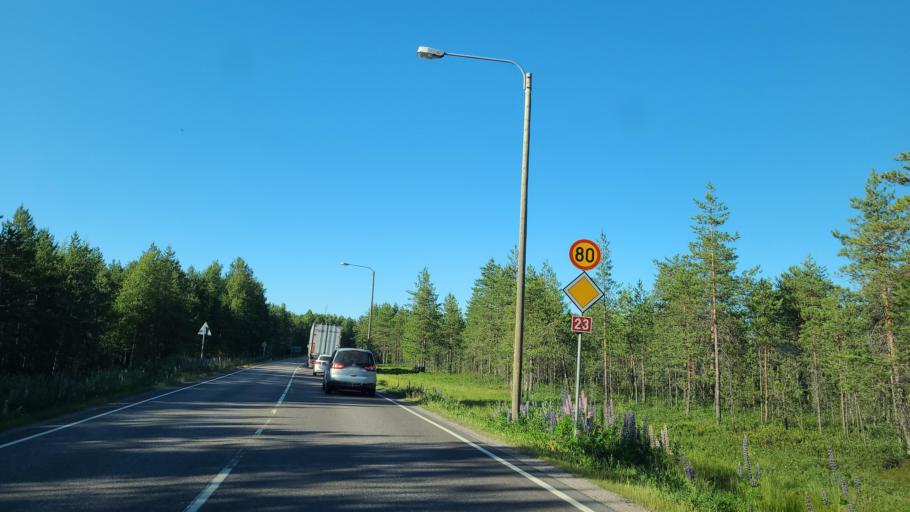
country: FI
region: Southern Savonia
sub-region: Pieksaemaeki
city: Pieksaemaeki
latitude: 62.2935
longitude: 27.1867
